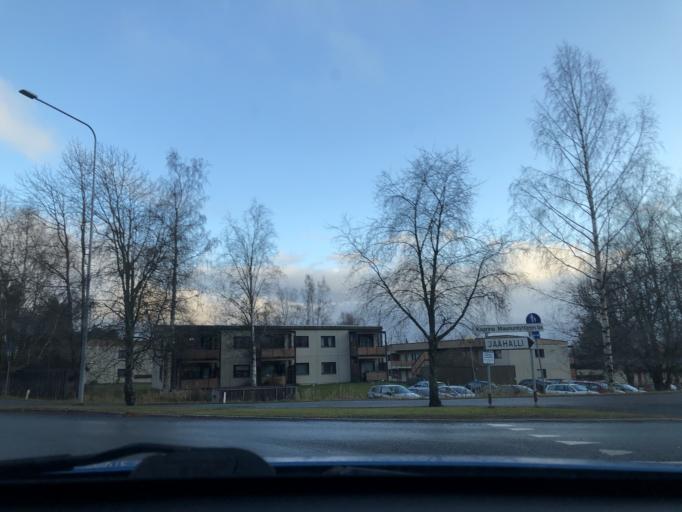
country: FI
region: Pirkanmaa
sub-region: Tampere
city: Kangasala
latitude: 61.4691
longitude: 24.0398
